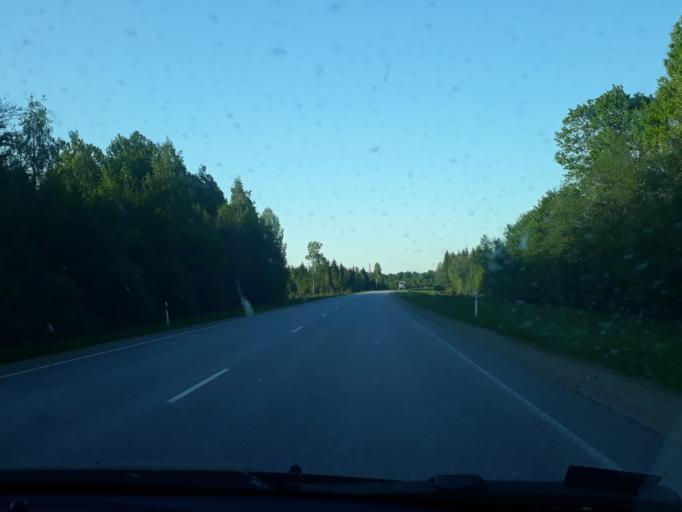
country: EE
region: Paernumaa
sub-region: Sindi linn
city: Sindi
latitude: 58.4634
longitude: 24.7025
